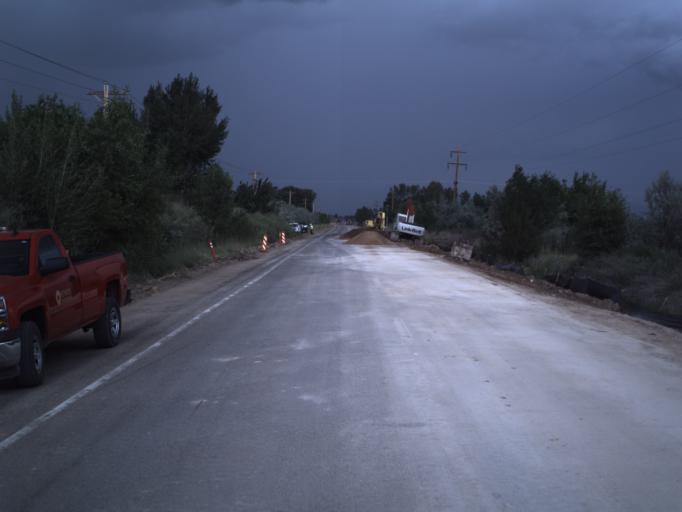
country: US
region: Utah
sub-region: Duchesne County
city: Roosevelt
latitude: 40.3917
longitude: -110.0298
